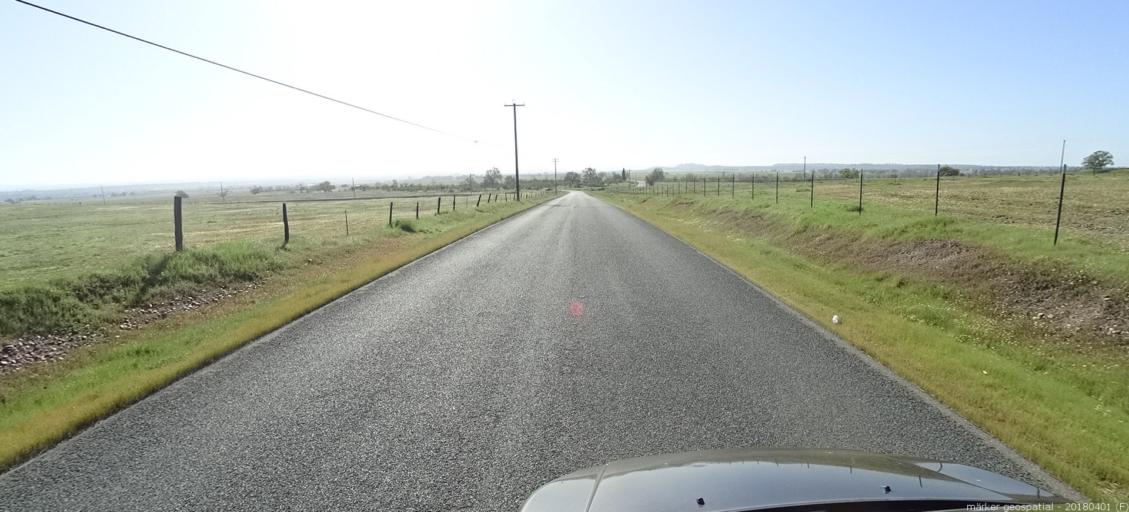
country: US
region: California
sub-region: Sacramento County
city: Rancho Murieta
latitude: 38.4290
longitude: -121.0575
